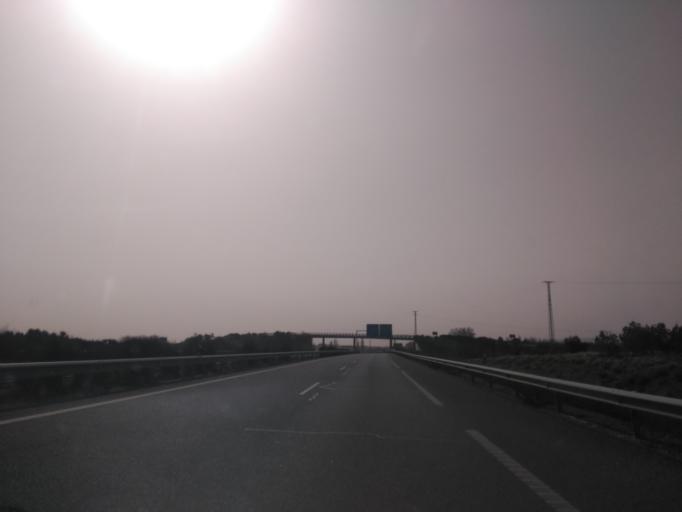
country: ES
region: Castille and Leon
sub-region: Provincia de Palencia
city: Villamuriel de Cerrato
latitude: 41.9536
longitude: -4.5035
